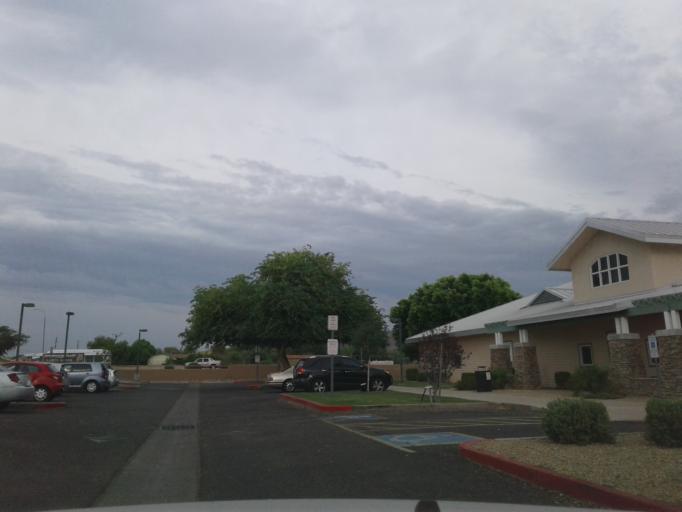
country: US
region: Arizona
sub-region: Maricopa County
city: Laveen
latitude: 33.3628
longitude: -112.0930
